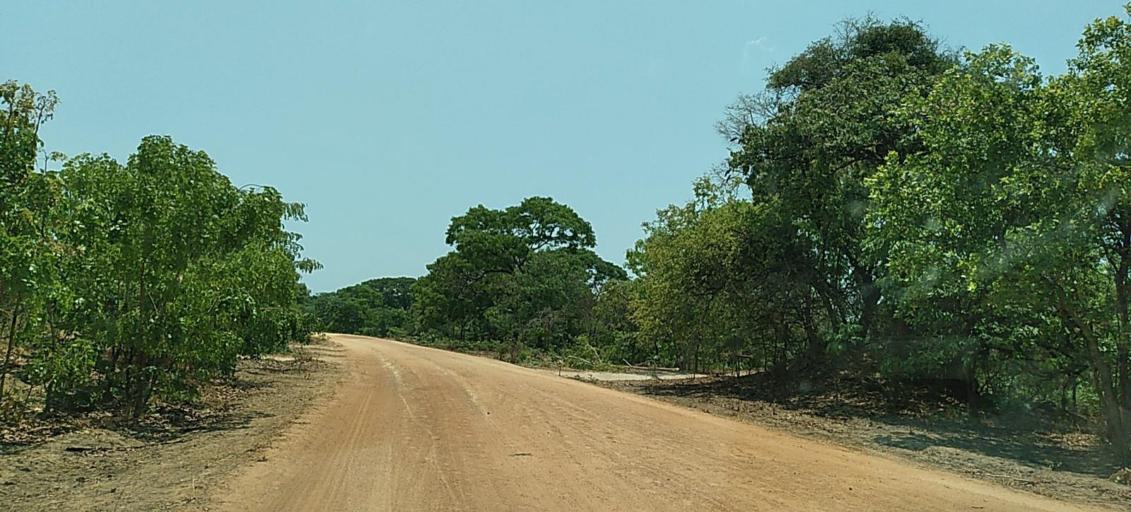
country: ZM
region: Copperbelt
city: Mpongwe
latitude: -13.8090
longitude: 27.8543
